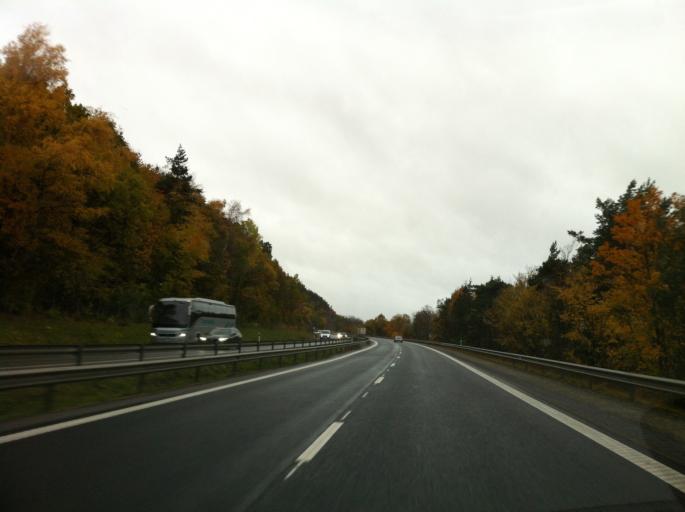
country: SE
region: Joenkoeping
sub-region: Jonkopings Kommun
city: Kaxholmen
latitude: 57.9106
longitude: 14.3034
